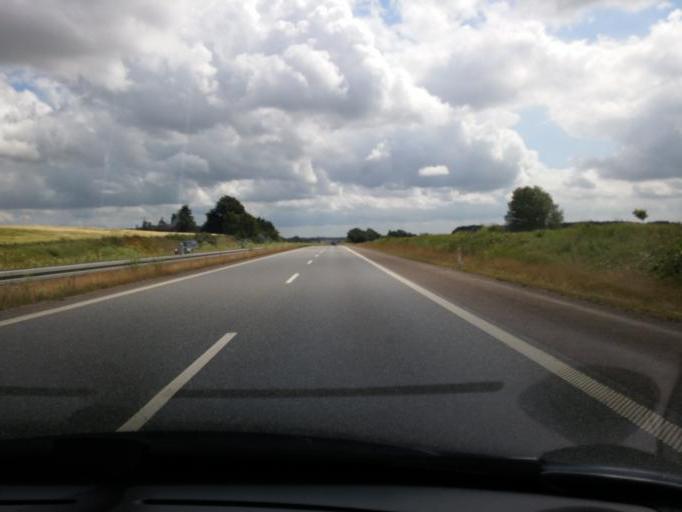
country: DK
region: South Denmark
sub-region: Faaborg-Midtfyn Kommune
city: Ringe
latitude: 55.2054
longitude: 10.5113
